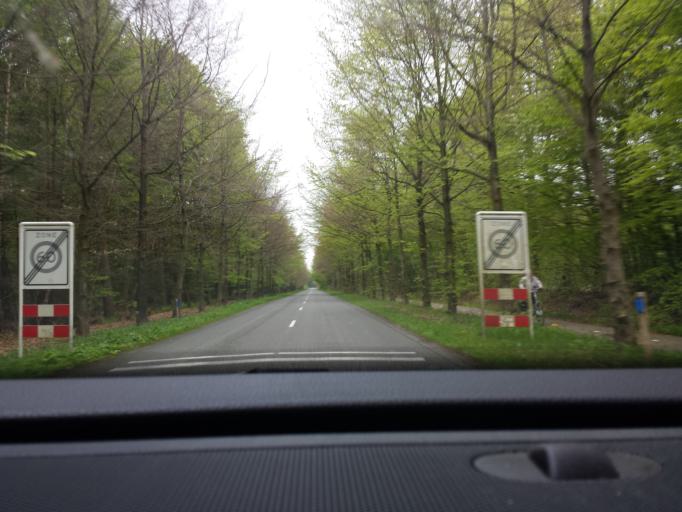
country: NL
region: Gelderland
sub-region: Gemeente Bronckhorst
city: Hengelo
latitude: 52.0674
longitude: 6.3704
